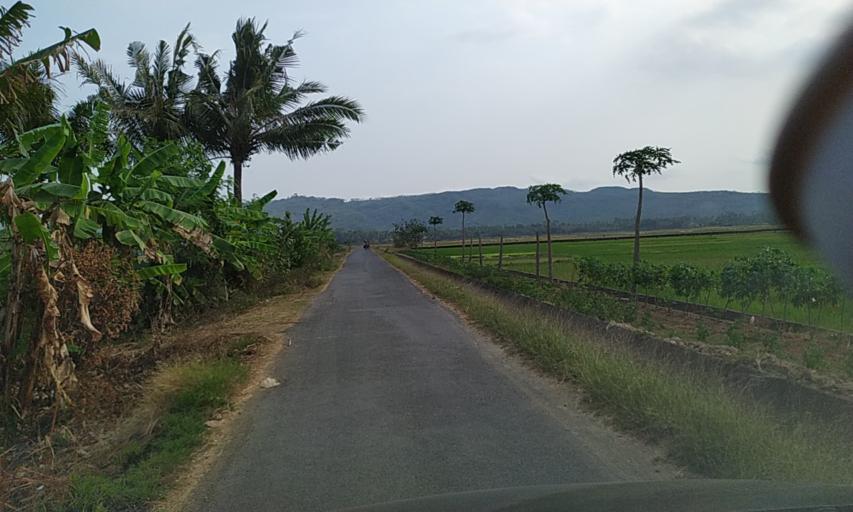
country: ID
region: Central Java
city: Mulyadadi
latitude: -7.3448
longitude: 108.7532
